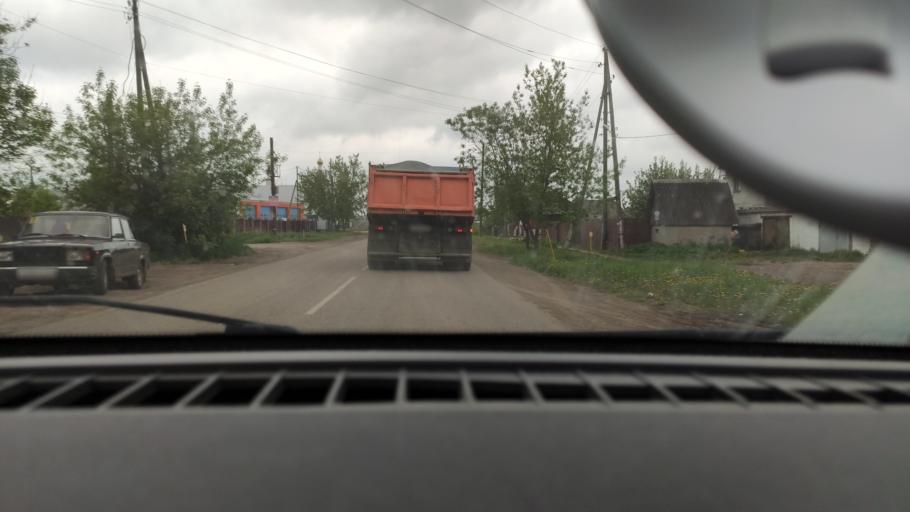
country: RU
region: Perm
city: Gamovo
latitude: 57.8682
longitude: 56.1023
